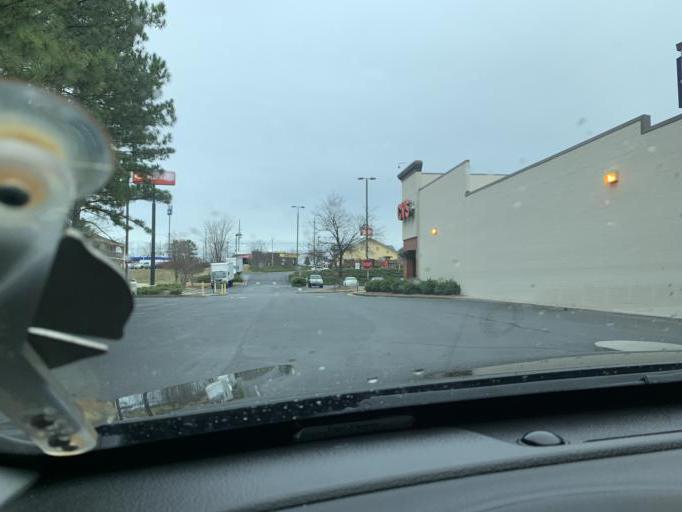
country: US
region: Georgia
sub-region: Cobb County
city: Acworth
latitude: 34.0744
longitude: -84.6531
